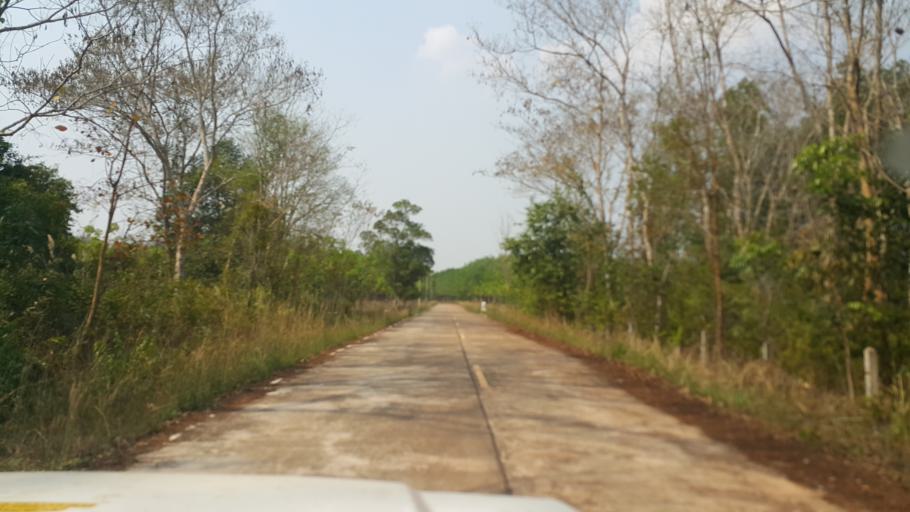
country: TH
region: Nakhon Phanom
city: Ban Phaeng
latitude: 17.9650
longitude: 104.1546
